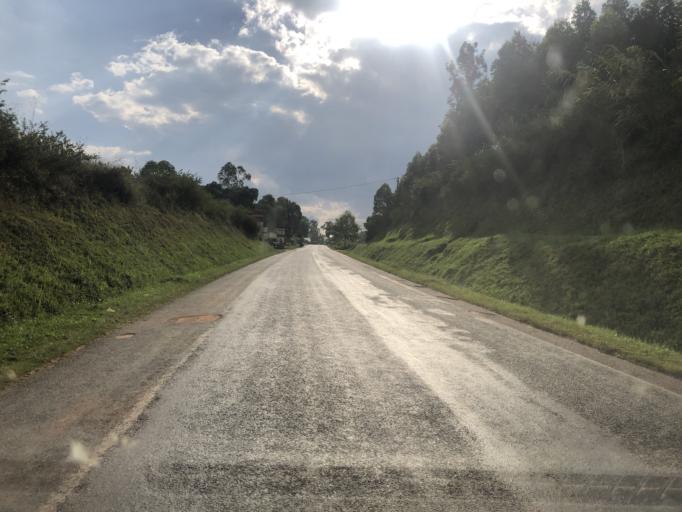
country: UG
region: Western Region
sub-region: Bushenyi District
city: Bushenyi
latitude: -0.5430
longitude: 30.2041
